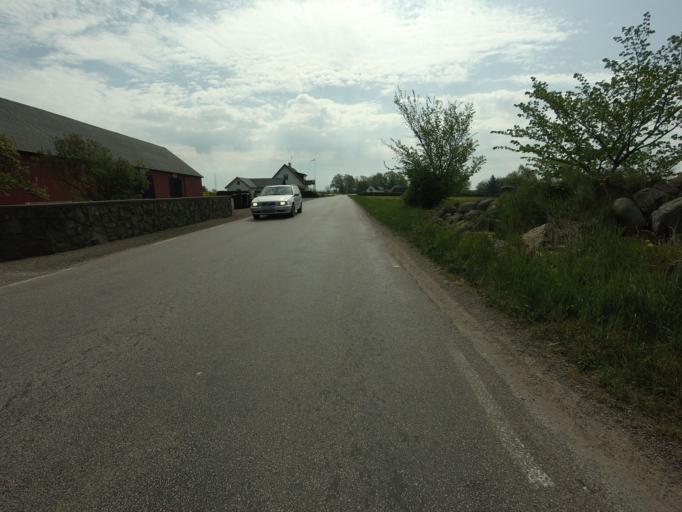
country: SE
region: Skane
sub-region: Hoganas Kommun
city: Hoganas
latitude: 56.1933
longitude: 12.6040
